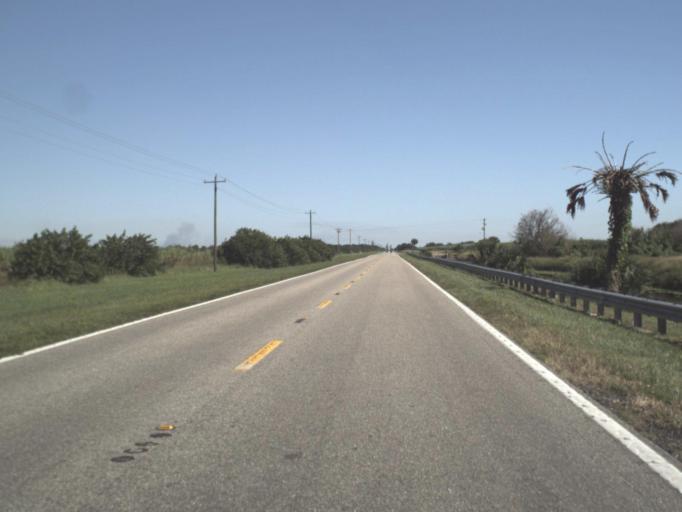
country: US
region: Florida
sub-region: Glades County
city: Moore Haven
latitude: 26.7633
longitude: -81.1646
